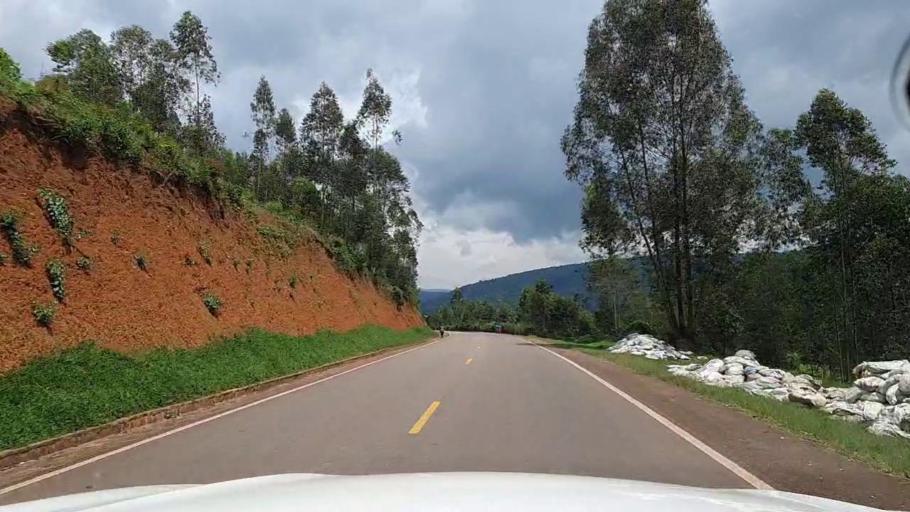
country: RW
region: Kigali
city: Kigali
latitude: -1.7996
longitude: 30.1288
